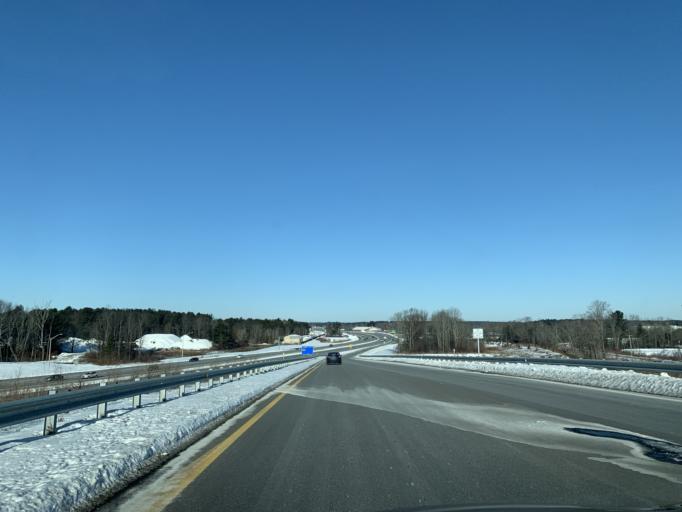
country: US
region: Maine
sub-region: York County
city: South Eliot
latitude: 43.1047
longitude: -70.8124
